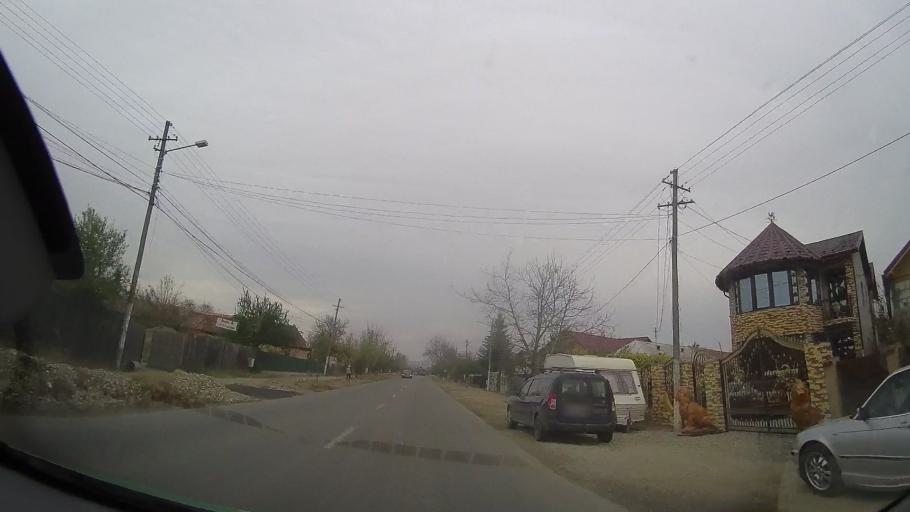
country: RO
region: Prahova
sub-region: Comuna Albesti-Paleologu
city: Albesti-Paleologu
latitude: 44.9574
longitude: 26.2313
